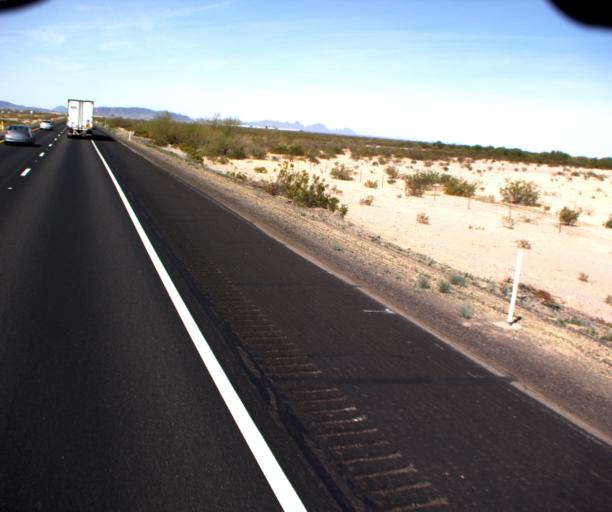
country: US
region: Arizona
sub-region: La Paz County
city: Salome
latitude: 33.6264
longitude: -113.7344
